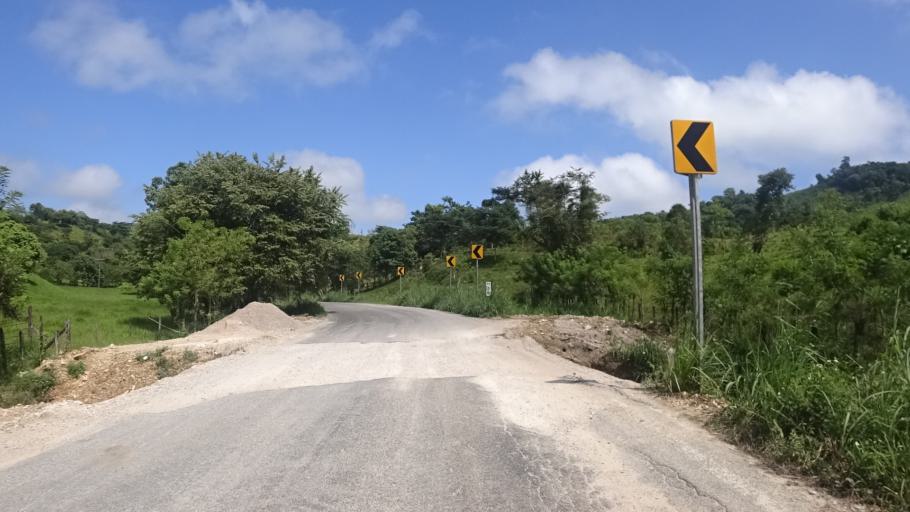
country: MX
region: Chiapas
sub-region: Palenque
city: Doctor Samuel Leon Brindis
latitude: 17.4504
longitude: -91.9617
